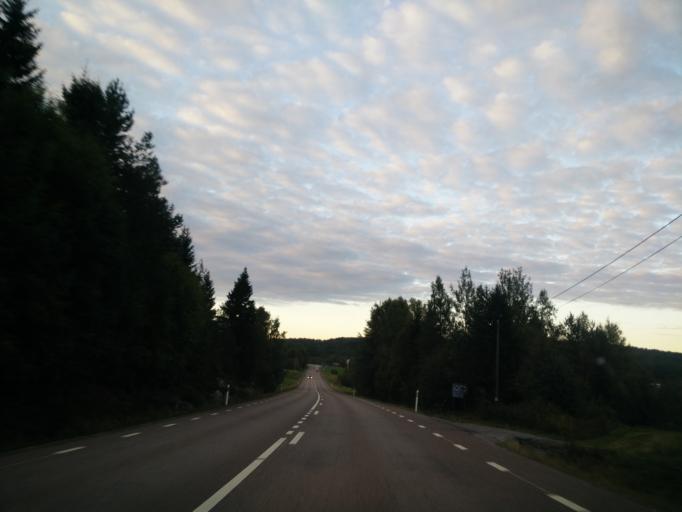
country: SE
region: Vaesternorrland
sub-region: Kramfors Kommun
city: Nordingra
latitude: 62.9252
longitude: 18.0805
